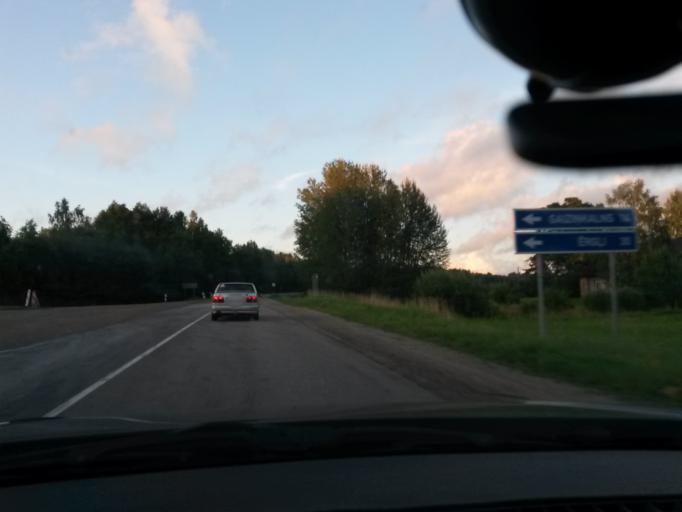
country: LV
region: Madonas Rajons
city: Madona
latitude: 56.8047
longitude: 26.0440
